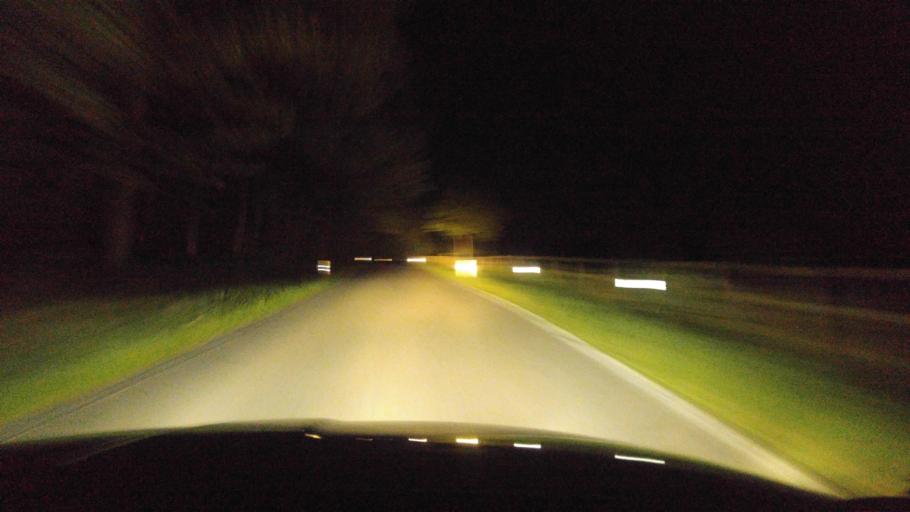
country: DE
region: North Rhine-Westphalia
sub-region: Regierungsbezirk Koln
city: Numbrecht
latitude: 50.8902
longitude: 7.5407
